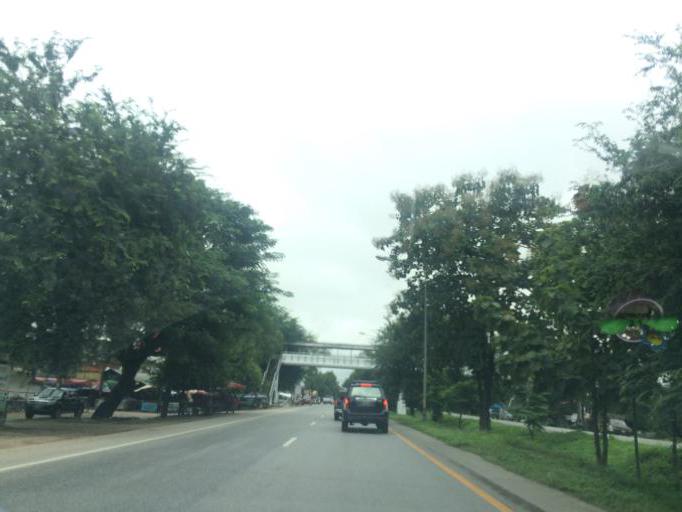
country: TH
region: Chiang Rai
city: Mae Lao
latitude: 19.7739
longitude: 99.7390
